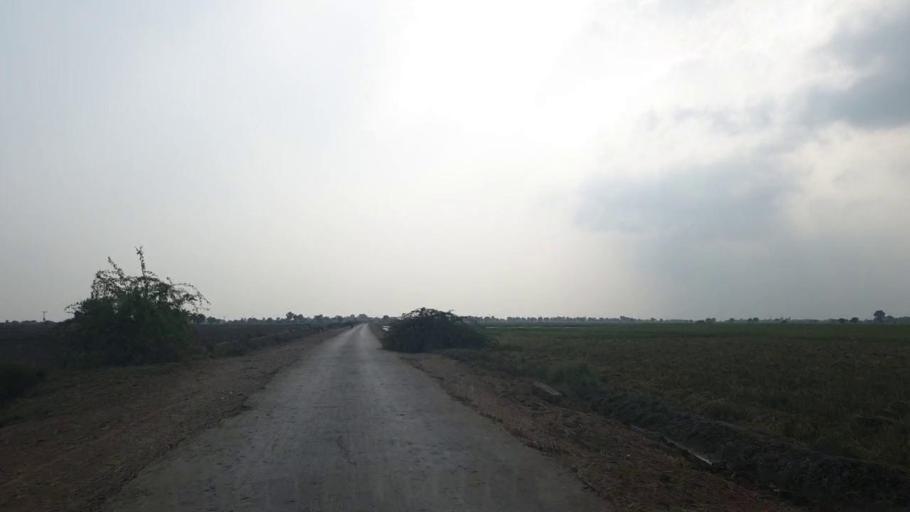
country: PK
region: Sindh
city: Badin
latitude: 24.6494
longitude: 68.6992
